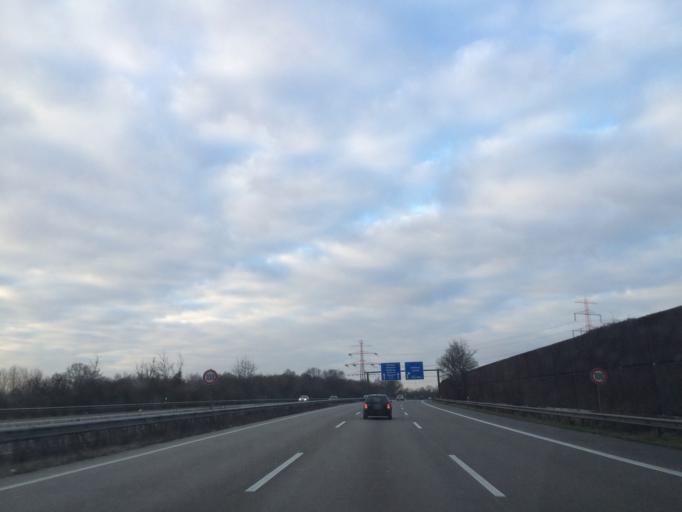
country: DE
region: Schleswig-Holstein
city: Barsbuettel
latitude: 53.5671
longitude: 10.1886
